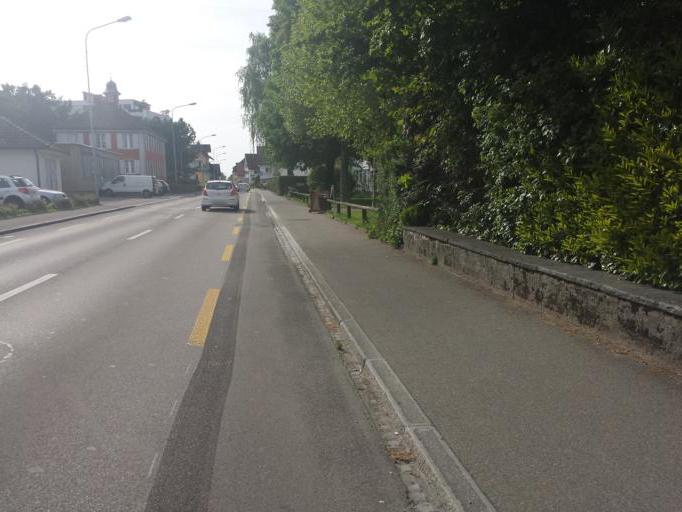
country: CH
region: Saint Gallen
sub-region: Wahlkreis Rorschach
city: Horn
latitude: 47.4950
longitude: 9.4669
